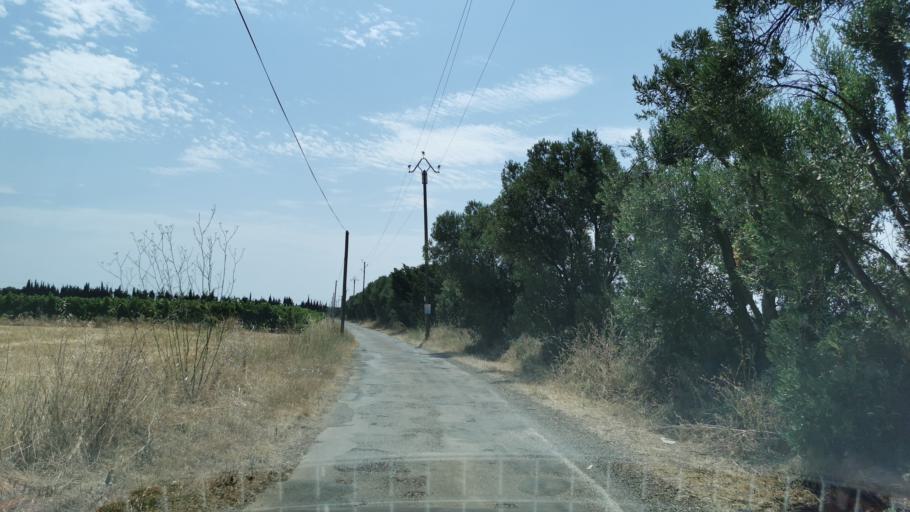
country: FR
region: Languedoc-Roussillon
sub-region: Departement de l'Aude
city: Bize-Minervois
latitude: 43.2929
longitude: 2.8853
